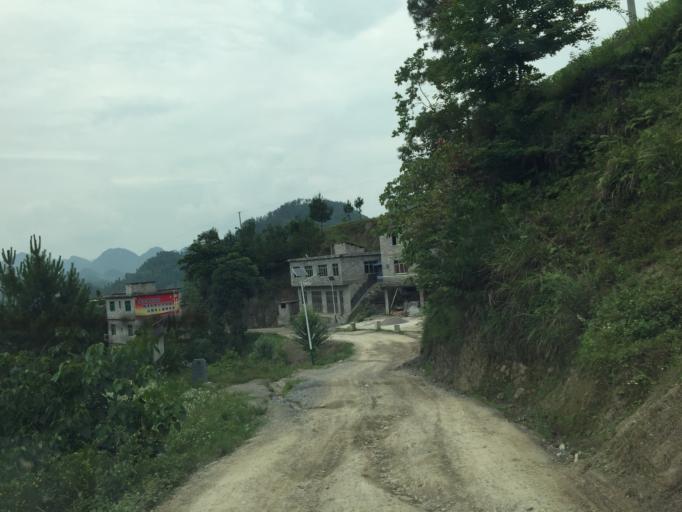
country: CN
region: Guizhou Sheng
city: Tongjing
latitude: 28.3714
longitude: 108.2569
